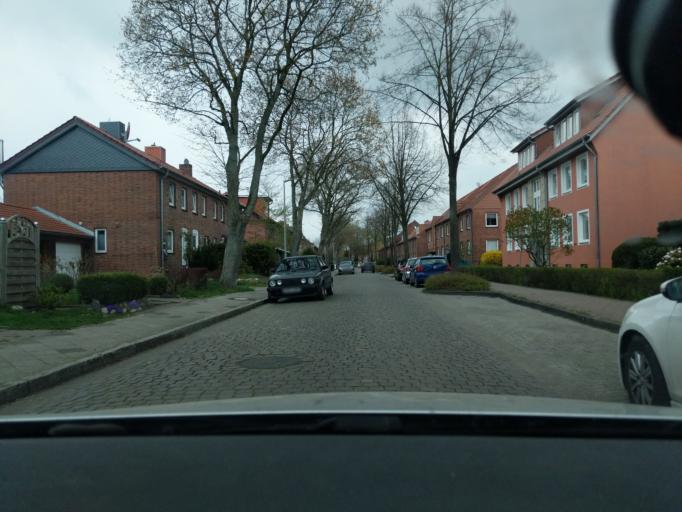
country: DE
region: Lower Saxony
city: Stade
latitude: 53.5893
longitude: 9.4637
